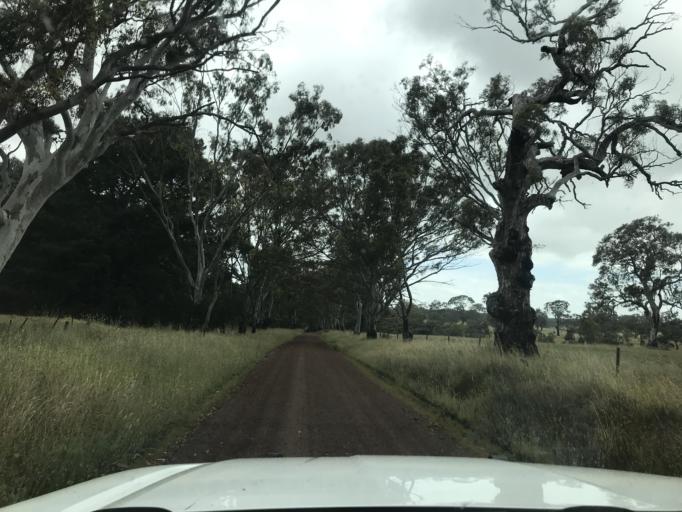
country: AU
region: South Australia
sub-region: Wattle Range
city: Penola
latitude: -37.2345
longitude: 141.4447
